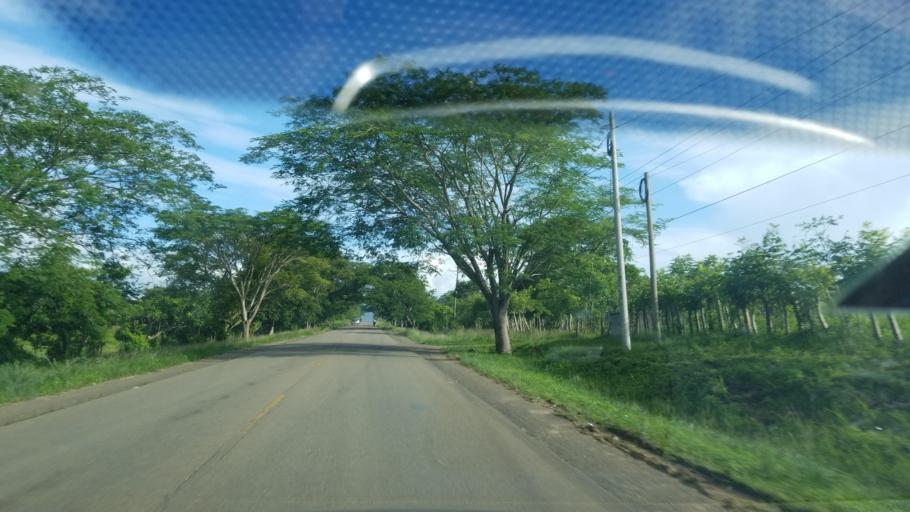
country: HN
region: El Paraiso
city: Arauli
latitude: 13.9211
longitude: -86.5577
